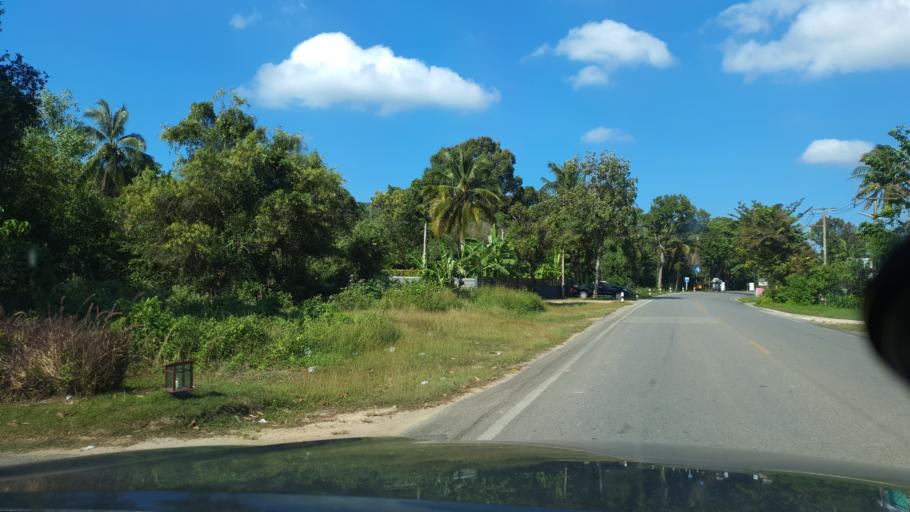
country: TH
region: Krabi
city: Krabi
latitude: 8.0276
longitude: 98.8724
